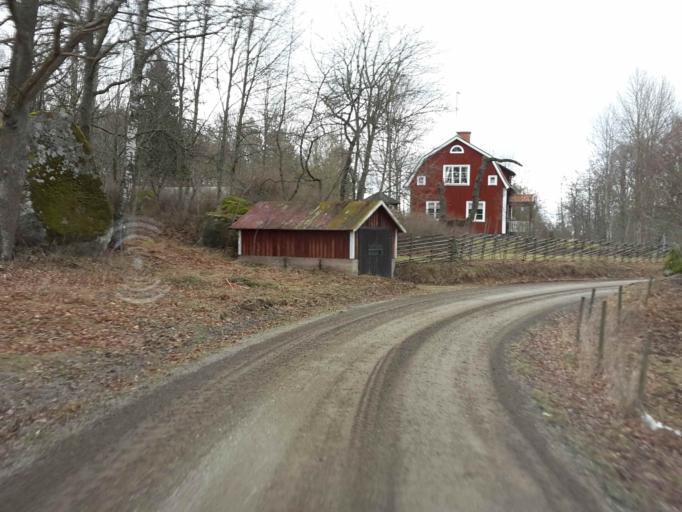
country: SE
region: OEstergoetland
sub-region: Atvidabergs Kommun
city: Atvidaberg
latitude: 58.2026
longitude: 15.8549
